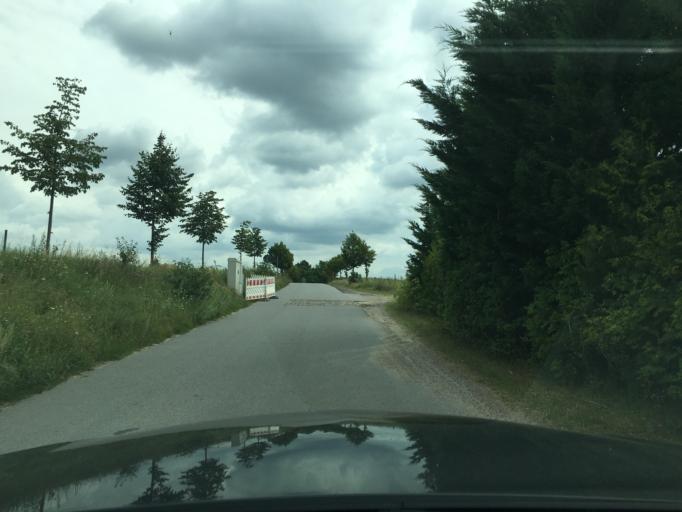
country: DE
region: Mecklenburg-Vorpommern
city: Waren
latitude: 53.4868
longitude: 12.7374
